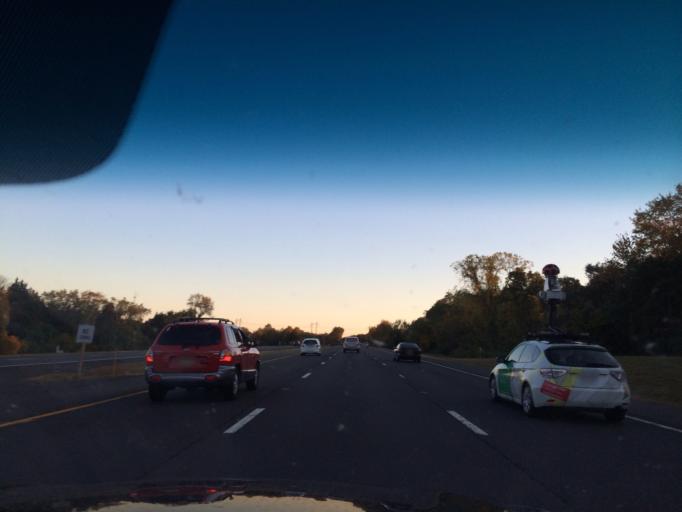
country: US
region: New Jersey
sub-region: Monmouth County
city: Tinton Falls
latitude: 40.2946
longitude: -74.0922
